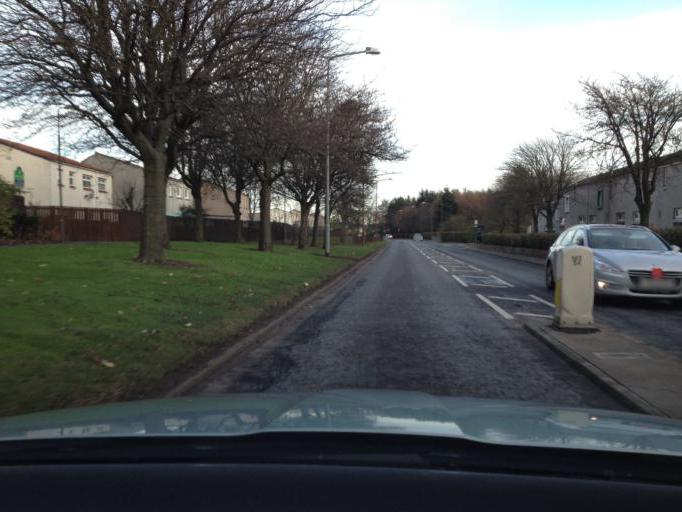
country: GB
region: Scotland
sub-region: West Lothian
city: Mid Calder
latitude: 55.8935
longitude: -3.4946
